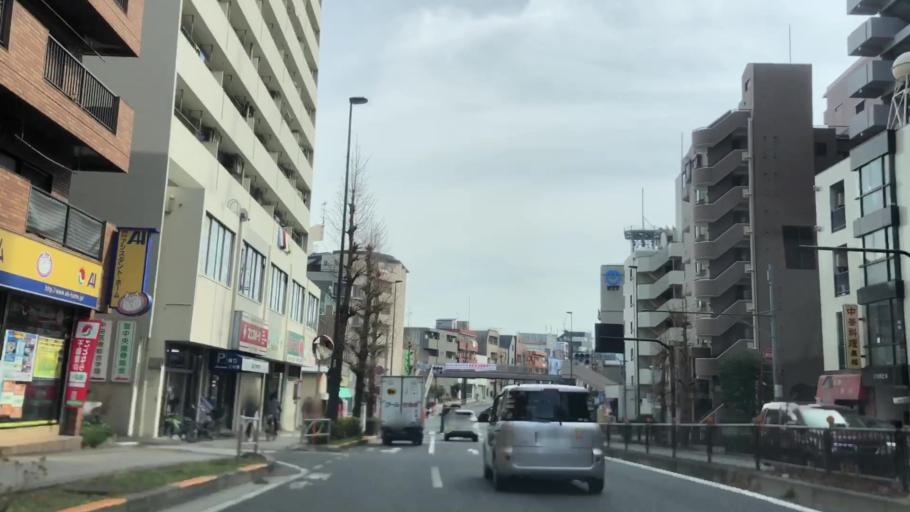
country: JP
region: Saitama
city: Wako
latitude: 35.7757
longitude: 139.6335
